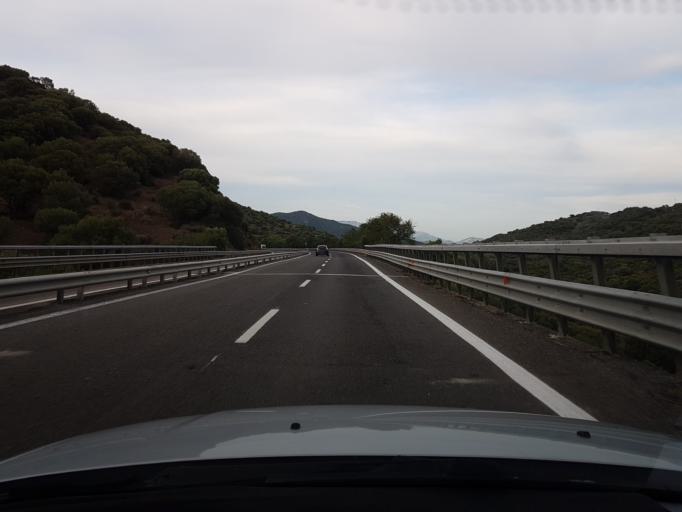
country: IT
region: Sardinia
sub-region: Provincia di Nuoro
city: Nuoro
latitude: 40.3533
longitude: 9.3428
